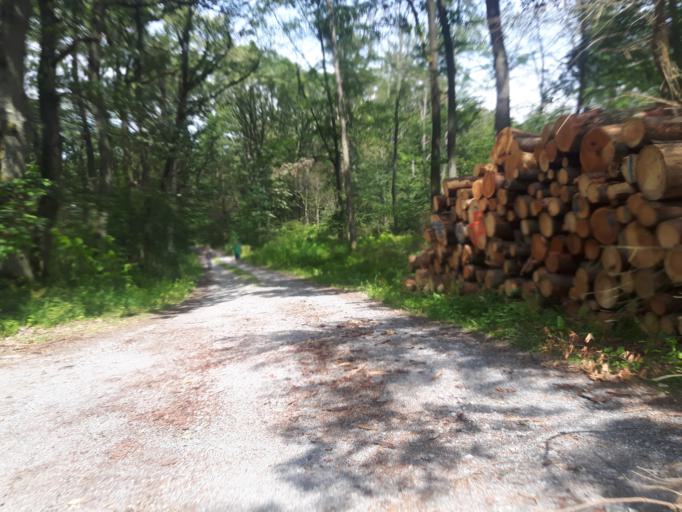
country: DE
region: Baden-Wuerttemberg
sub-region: Regierungsbezirk Stuttgart
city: Pfaffenhofen
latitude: 49.0401
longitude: 8.9561
